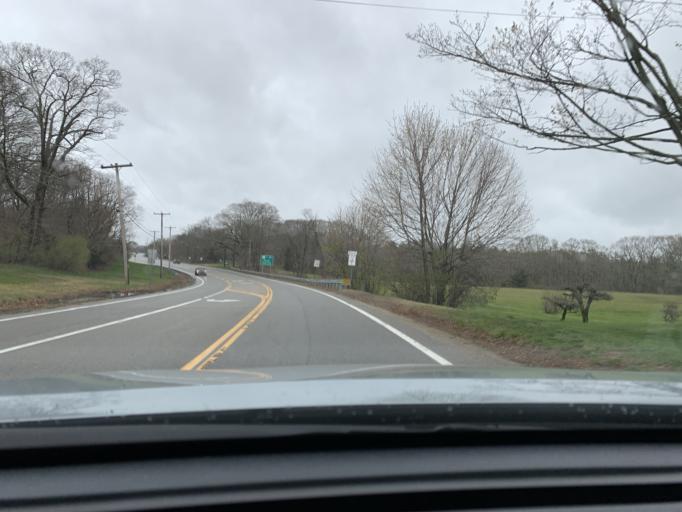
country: US
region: Rhode Island
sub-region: Washington County
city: Exeter
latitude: 41.6079
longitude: -71.4928
